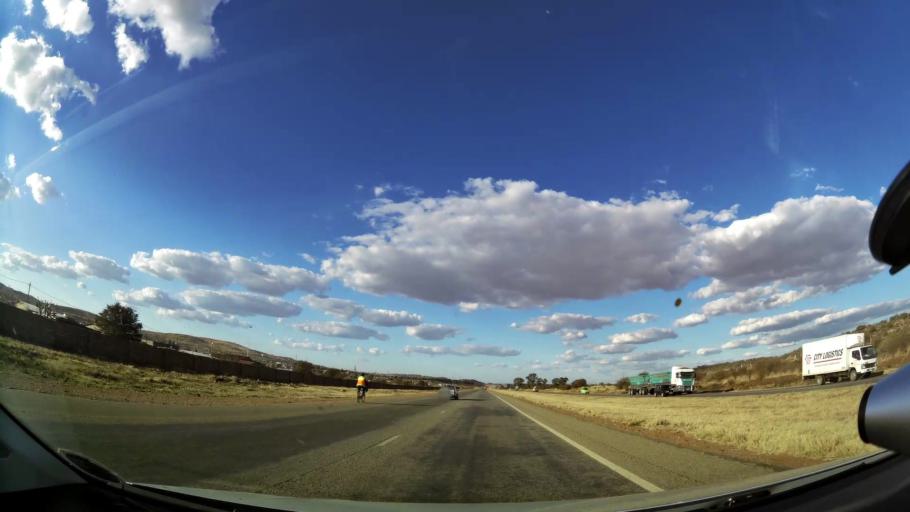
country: ZA
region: North-West
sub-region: Dr Kenneth Kaunda District Municipality
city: Potchefstroom
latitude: -26.7498
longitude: 27.0216
